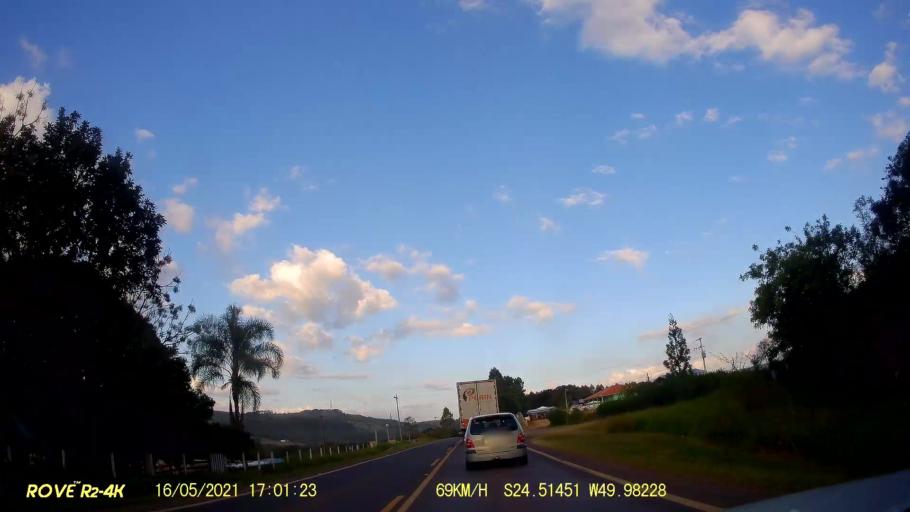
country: BR
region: Parana
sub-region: Pirai Do Sul
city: Pirai do Sul
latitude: -24.5145
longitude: -49.9823
